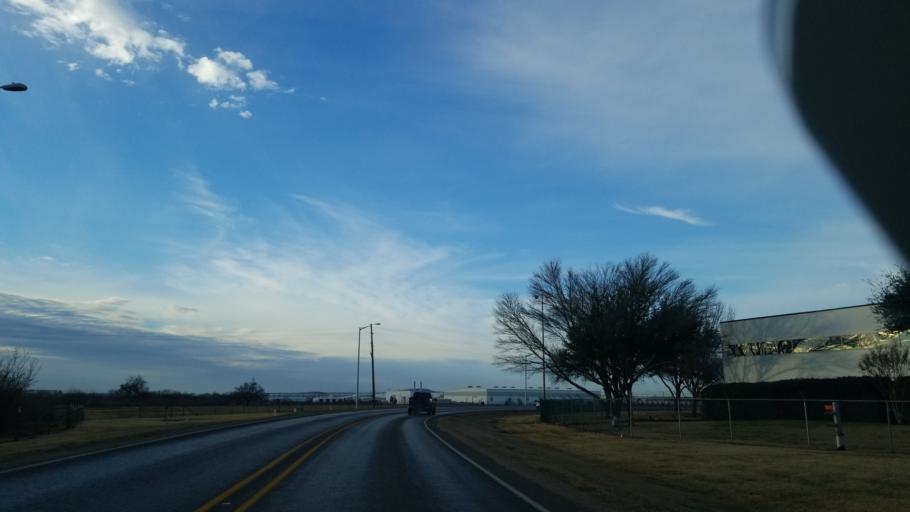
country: US
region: Texas
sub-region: Denton County
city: Denton
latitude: 33.2030
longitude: -97.1738
